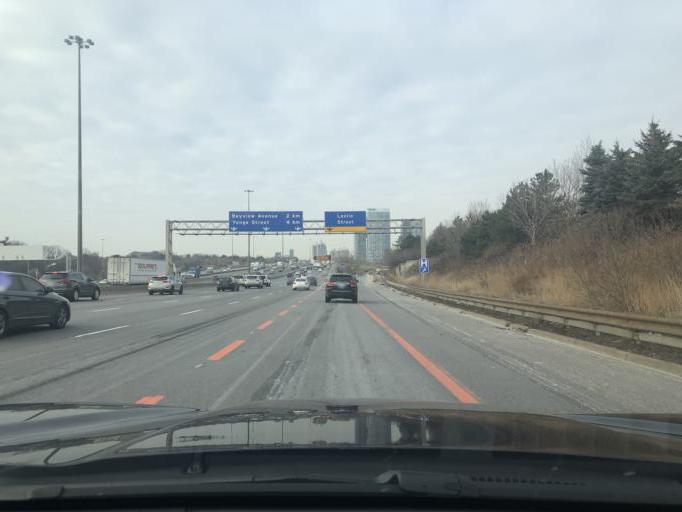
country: CA
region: Ontario
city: Willowdale
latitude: 43.7670
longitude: -79.3558
